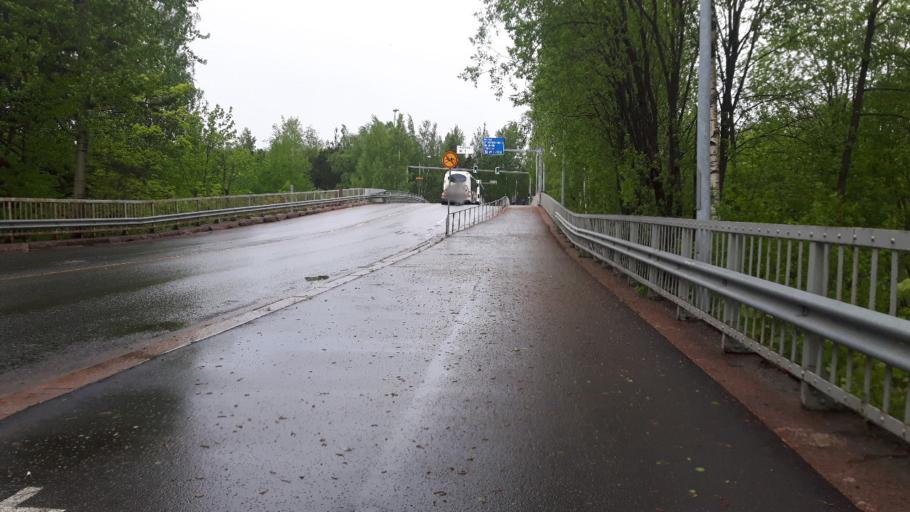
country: FI
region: Kymenlaakso
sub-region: Kotka-Hamina
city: Kotka
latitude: 60.4729
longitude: 26.9198
